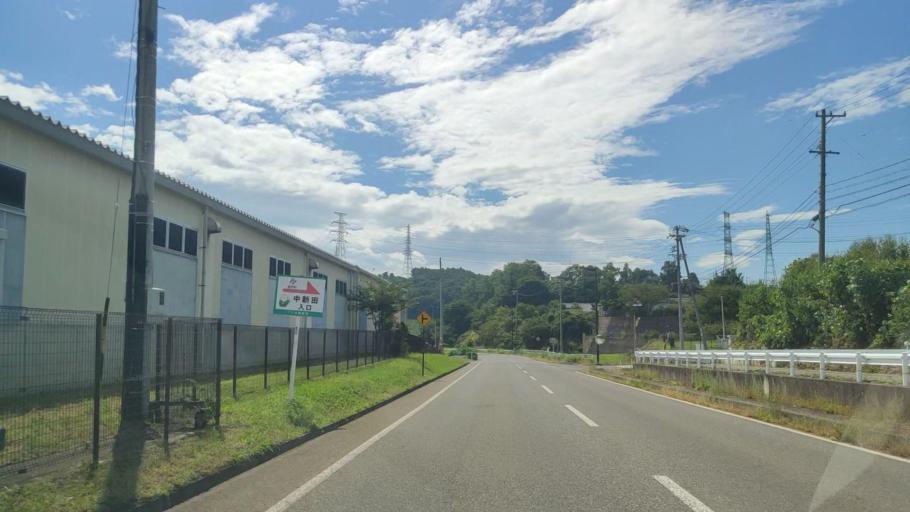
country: JP
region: Nagano
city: Nakano
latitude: 36.7388
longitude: 138.3052
